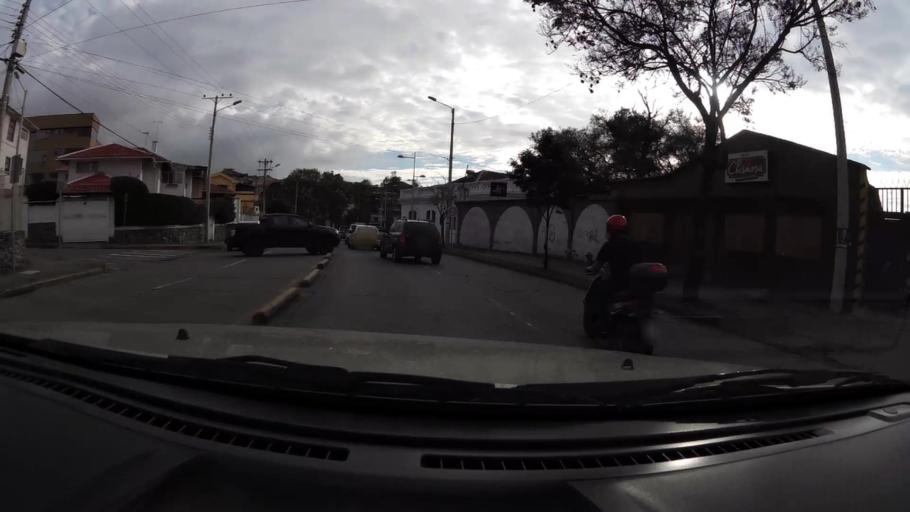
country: EC
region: El Oro
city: Zaruma
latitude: -3.5744
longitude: -79.5168
